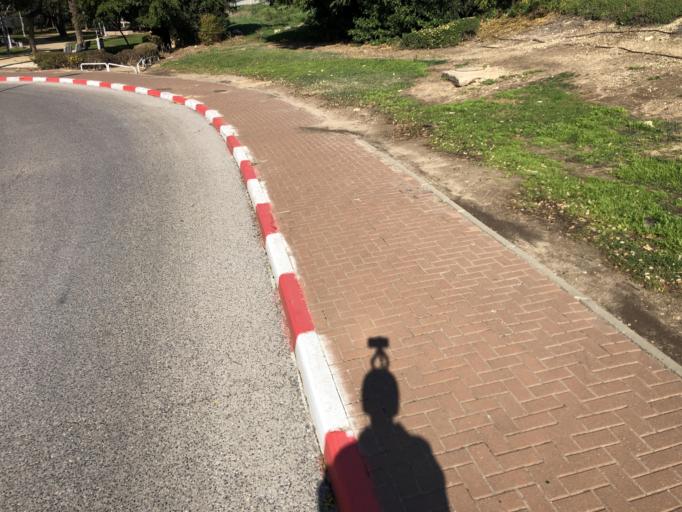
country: IL
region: Northern District
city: `Akko
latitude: 32.9244
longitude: 35.0969
